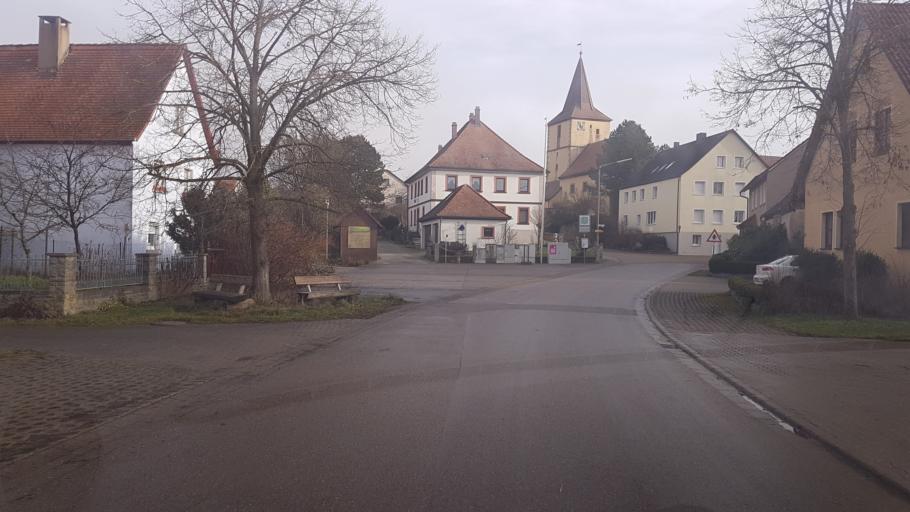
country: DE
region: Bavaria
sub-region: Regierungsbezirk Mittelfranken
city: Schnelldorf
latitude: 49.2386
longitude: 10.2046
